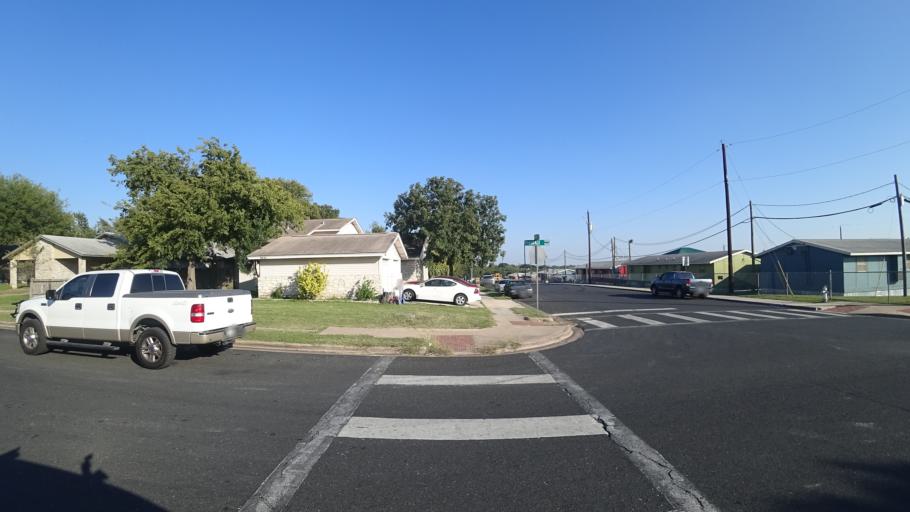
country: US
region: Texas
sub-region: Travis County
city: Wells Branch
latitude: 30.3565
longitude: -97.6800
